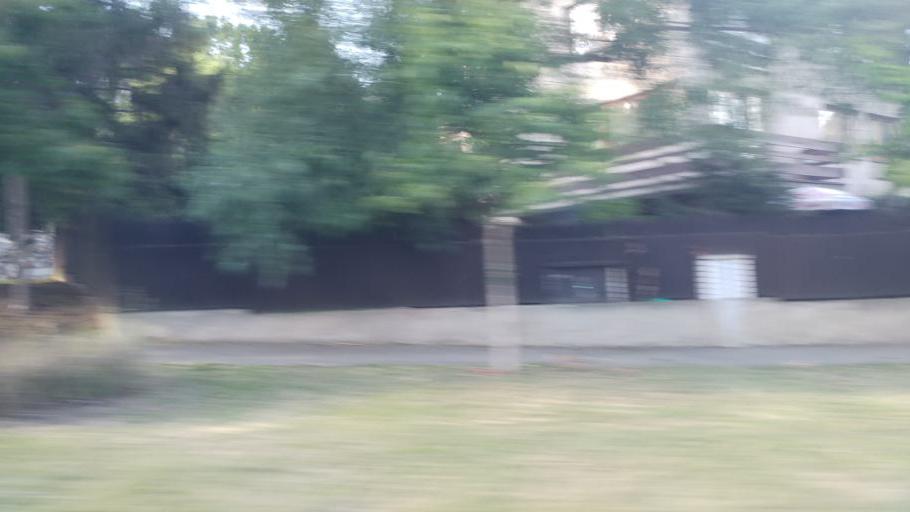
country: CZ
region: Praha
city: Prague
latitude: 50.1172
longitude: 14.4191
